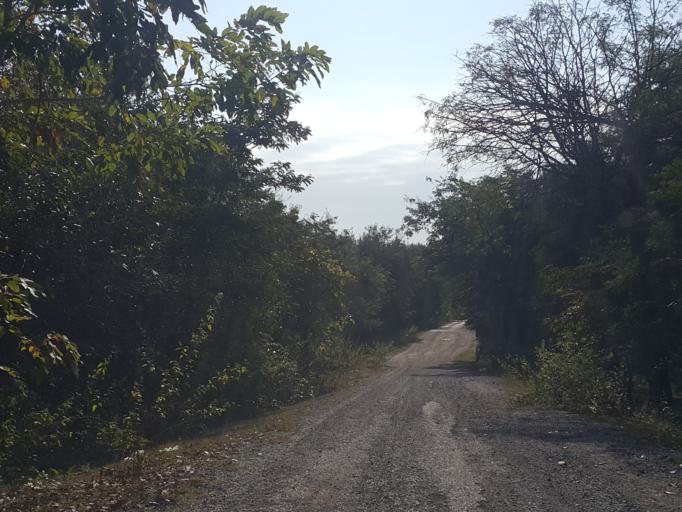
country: TH
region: Lampang
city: Mae Mo
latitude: 18.3114
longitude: 99.6560
